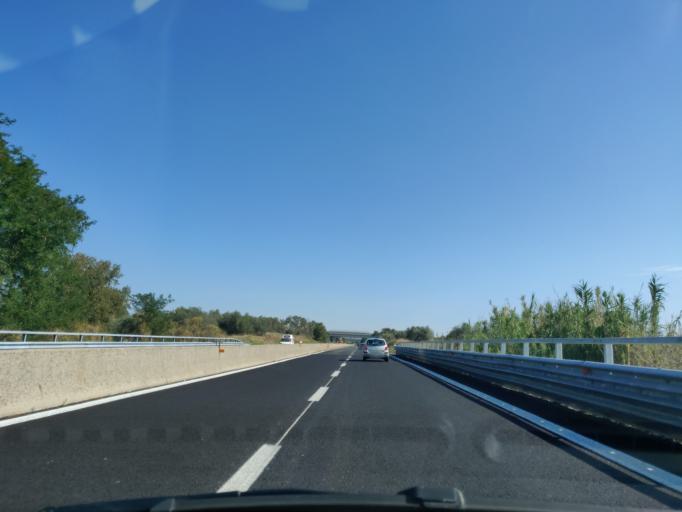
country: IT
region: Latium
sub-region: Provincia di Viterbo
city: Viterbo
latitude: 42.4082
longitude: 12.0721
